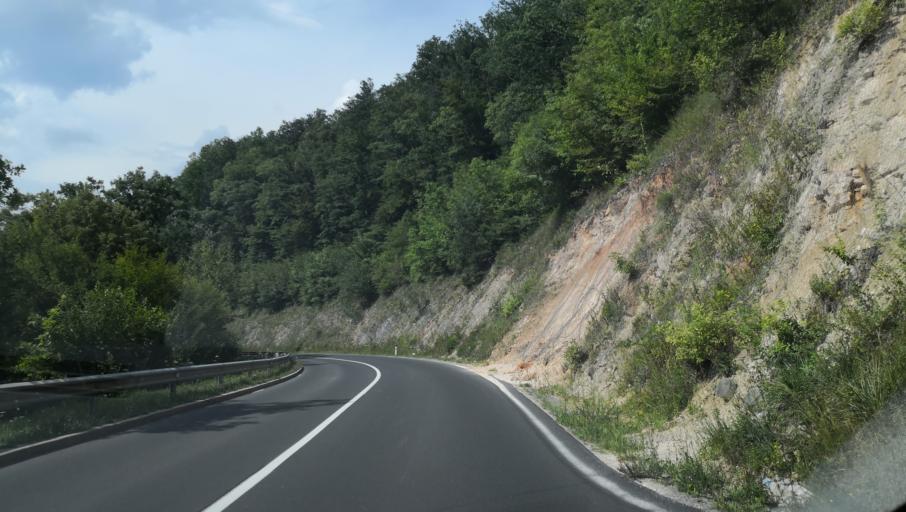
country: SI
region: Zuzemberk
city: Zuzemberk
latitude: 45.8450
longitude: 14.9060
